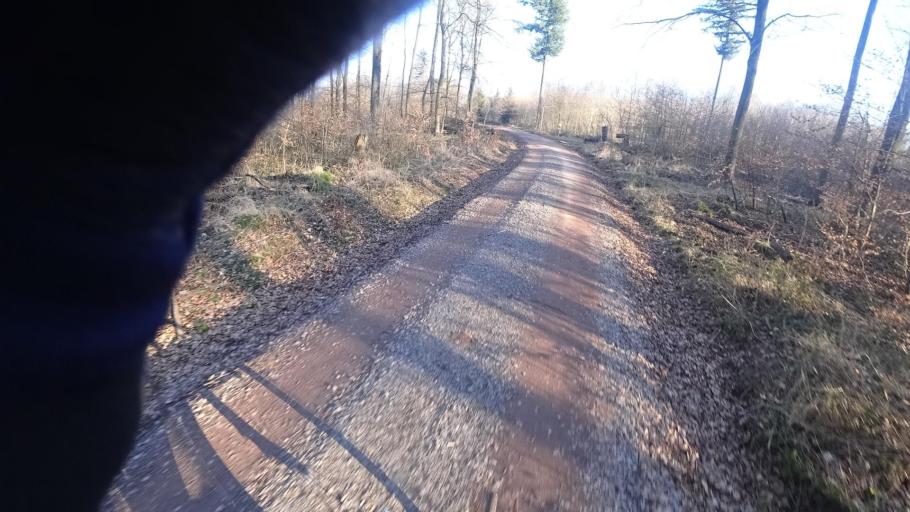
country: DE
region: Rheinland-Pfalz
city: Waldesch
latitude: 50.2601
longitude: 7.5450
